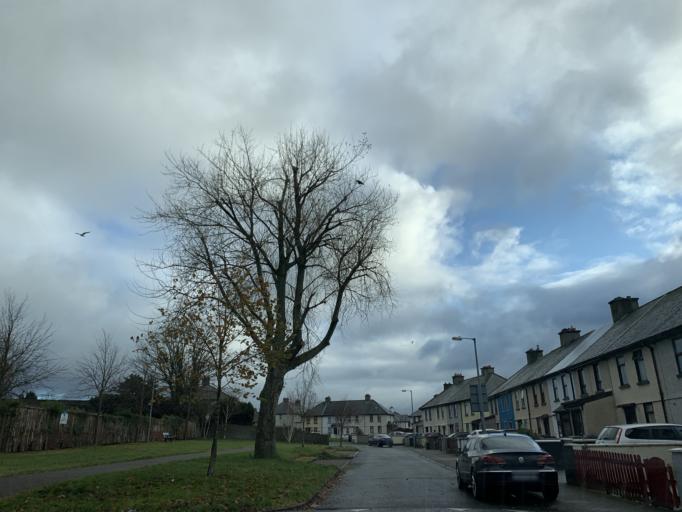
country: IE
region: Connaught
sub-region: Sligo
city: Sligo
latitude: 54.2693
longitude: -8.4631
